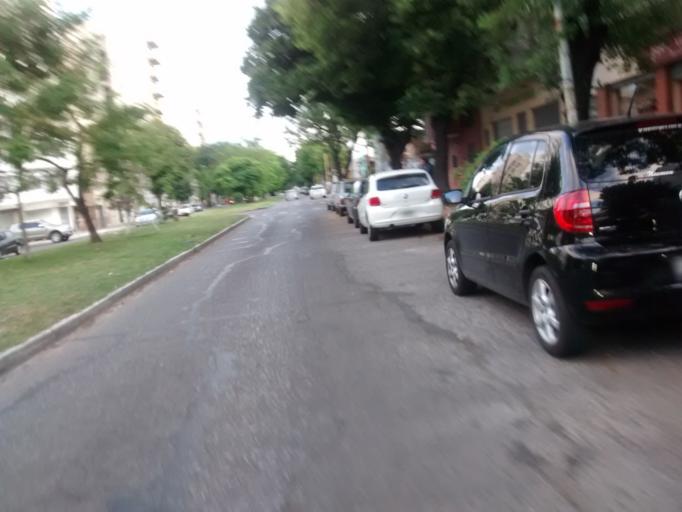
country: AR
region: Buenos Aires
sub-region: Partido de La Plata
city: La Plata
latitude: -34.9283
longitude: -57.9592
